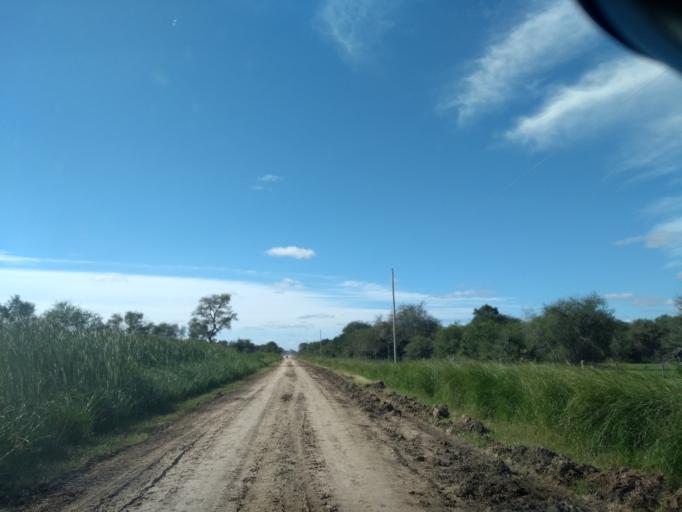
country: AR
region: Chaco
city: Colonia Benitez
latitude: -27.2875
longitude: -58.9318
